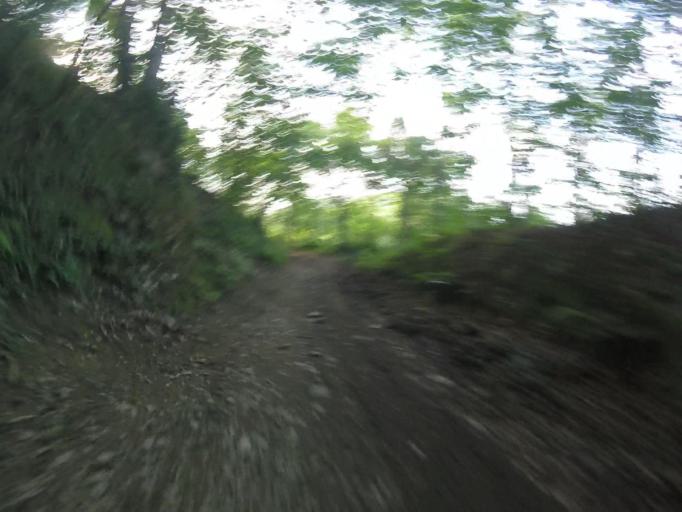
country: ES
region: Basque Country
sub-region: Provincia de Guipuzcoa
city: Irun
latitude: 43.3186
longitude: -1.7513
